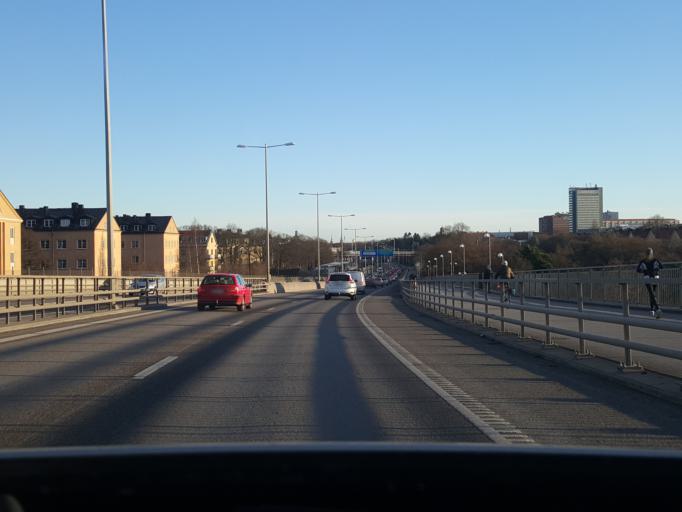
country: SE
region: Stockholm
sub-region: Solna Kommun
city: Solna
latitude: 59.3333
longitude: 17.9979
